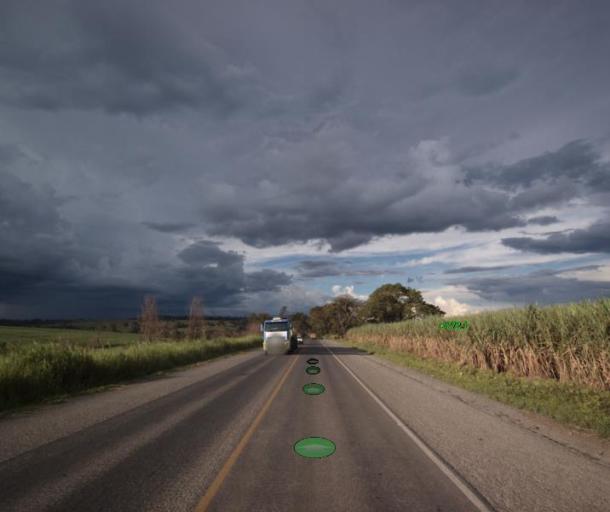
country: BR
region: Goias
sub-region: Itapaci
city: Itapaci
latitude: -15.0900
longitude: -49.4695
